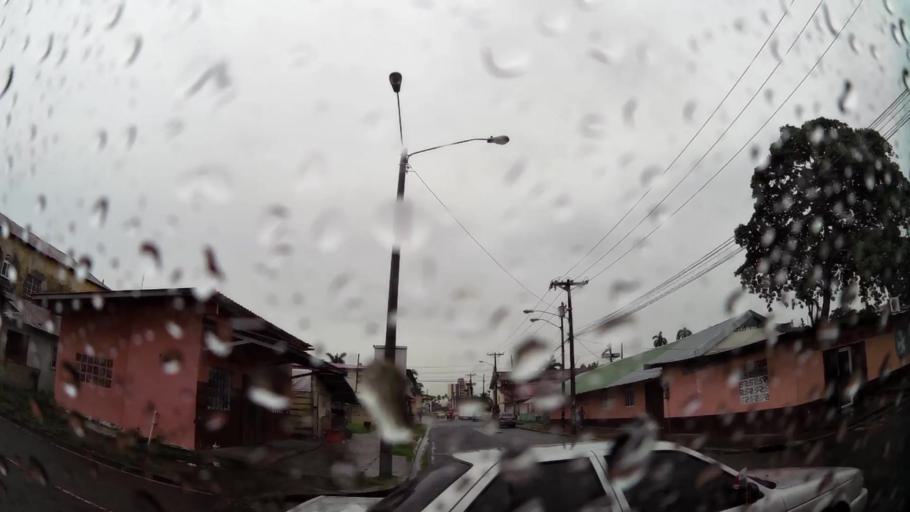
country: PA
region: Colon
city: Colon
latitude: 9.3631
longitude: -79.9044
